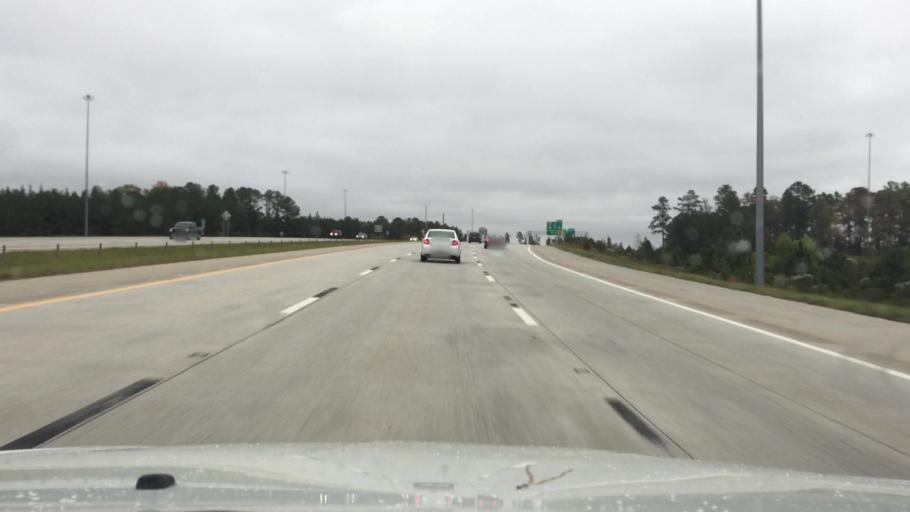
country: US
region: North Carolina
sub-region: Wake County
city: Green Level
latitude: 35.8378
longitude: -78.8890
